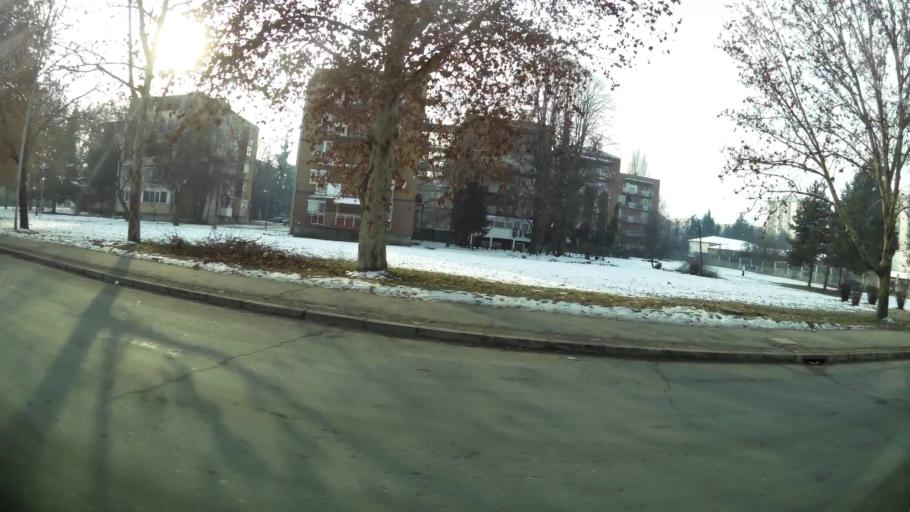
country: MK
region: Butel
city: Butel
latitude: 42.0250
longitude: 21.4437
